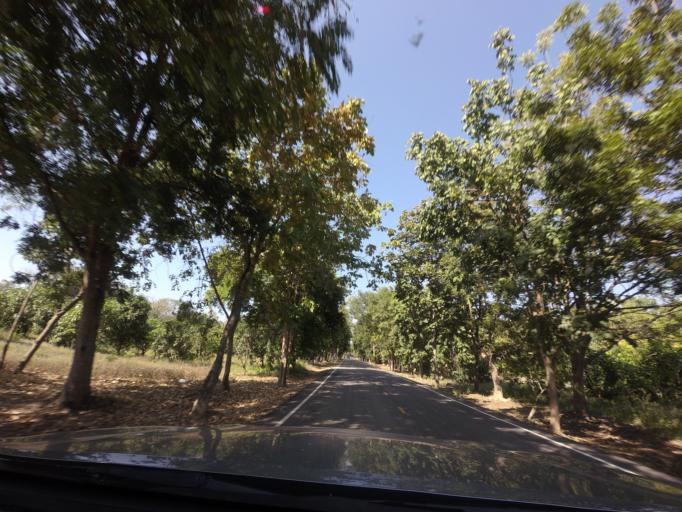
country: TH
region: Sukhothai
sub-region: Amphoe Si Satchanalai
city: Si Satchanalai
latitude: 17.4225
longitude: 99.7890
